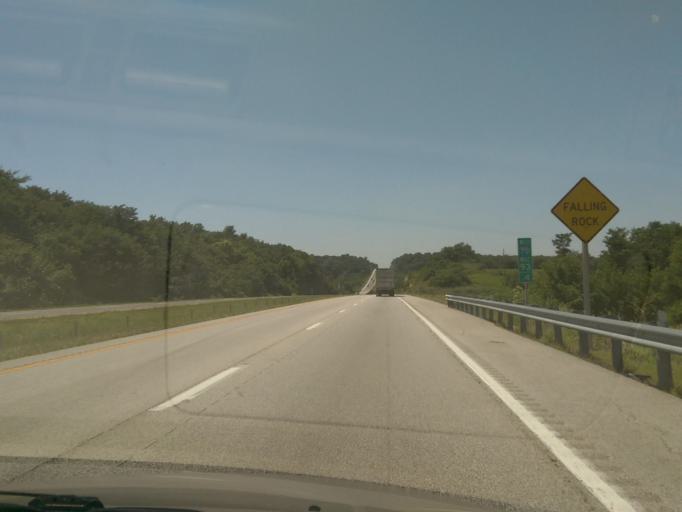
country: US
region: Missouri
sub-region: Cooper County
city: Boonville
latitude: 38.9342
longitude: -92.9350
